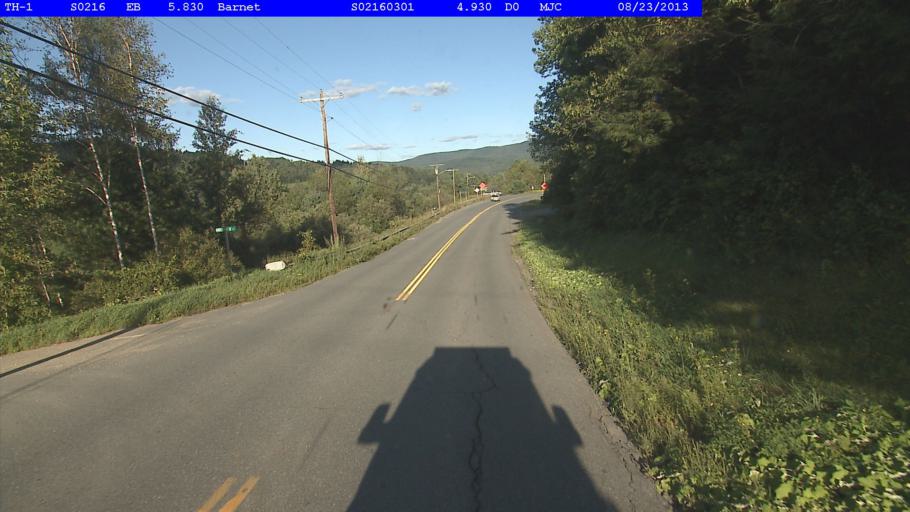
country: US
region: Vermont
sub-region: Caledonia County
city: Saint Johnsbury
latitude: 44.3005
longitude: -72.0621
